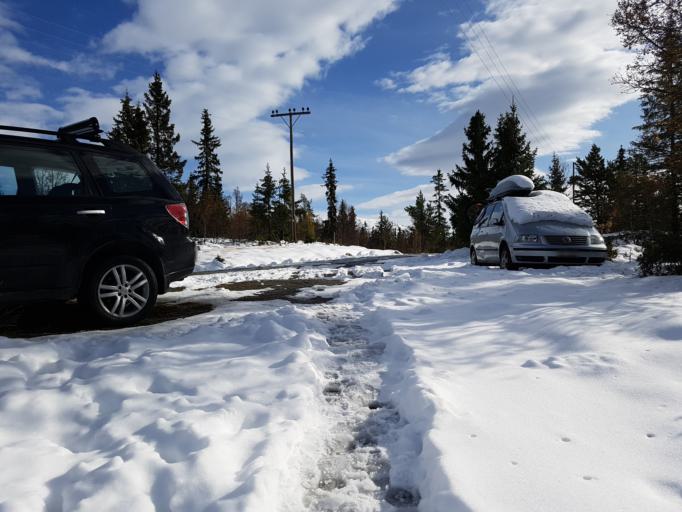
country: NO
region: Oppland
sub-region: Sel
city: Otta
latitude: 61.8160
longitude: 9.6780
